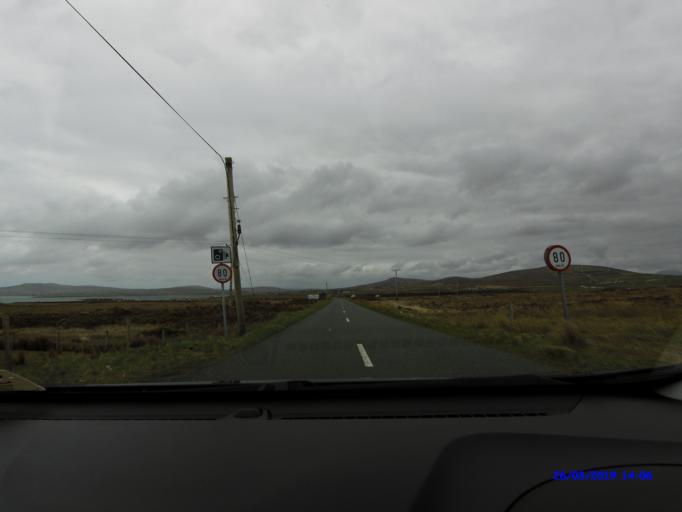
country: IE
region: Connaught
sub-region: Maigh Eo
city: Belmullet
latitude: 54.2070
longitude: -9.9272
